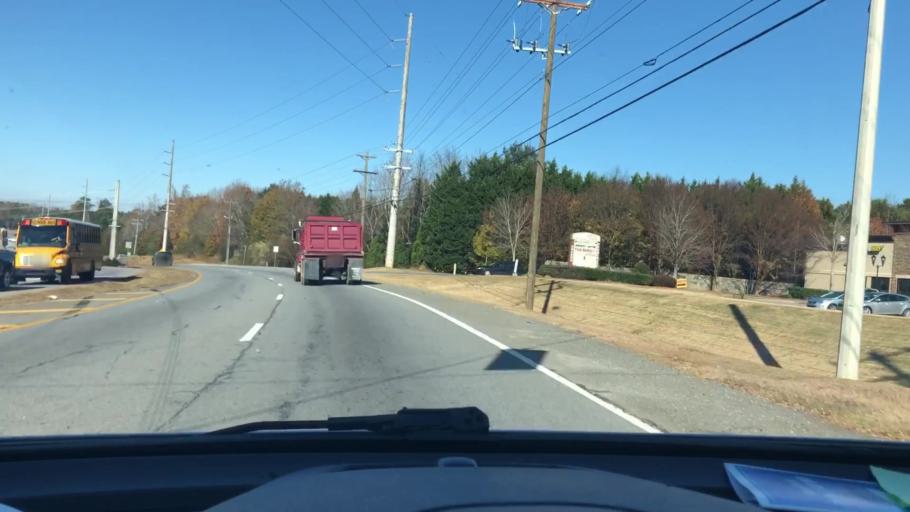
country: US
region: Georgia
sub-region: Forsyth County
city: Cumming
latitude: 34.1247
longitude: -84.1708
